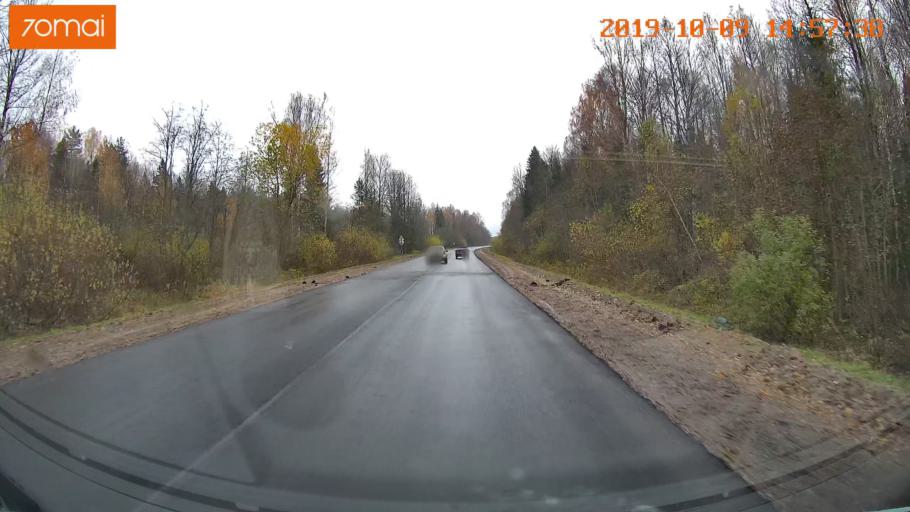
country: RU
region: Kostroma
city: Chistyye Bory
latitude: 58.3356
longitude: 41.6517
